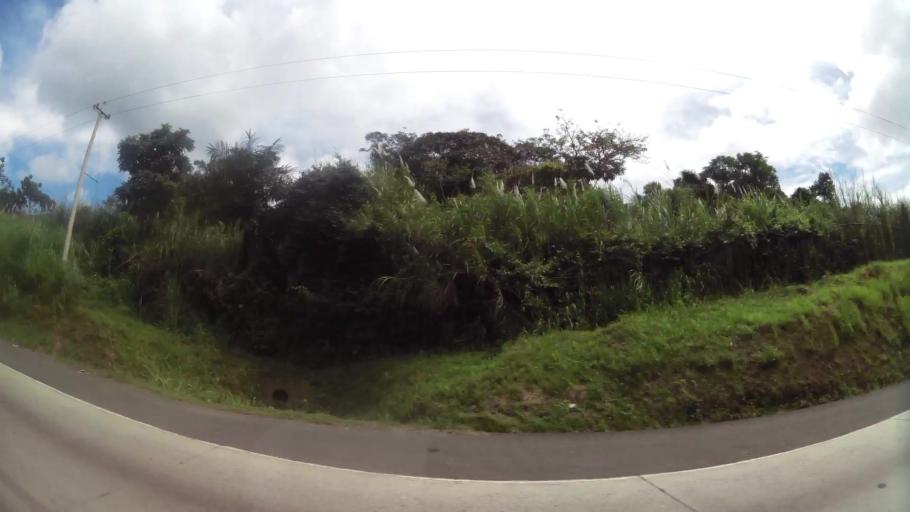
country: PA
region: Panama
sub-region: Distrito de Panama
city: Paraiso
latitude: 9.0040
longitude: -79.6492
